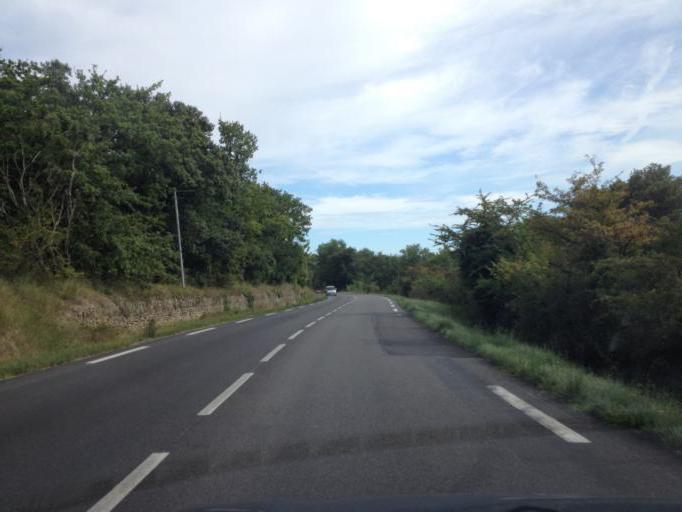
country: FR
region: Provence-Alpes-Cote d'Azur
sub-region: Departement du Vaucluse
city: Grillon
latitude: 44.4022
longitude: 4.9176
